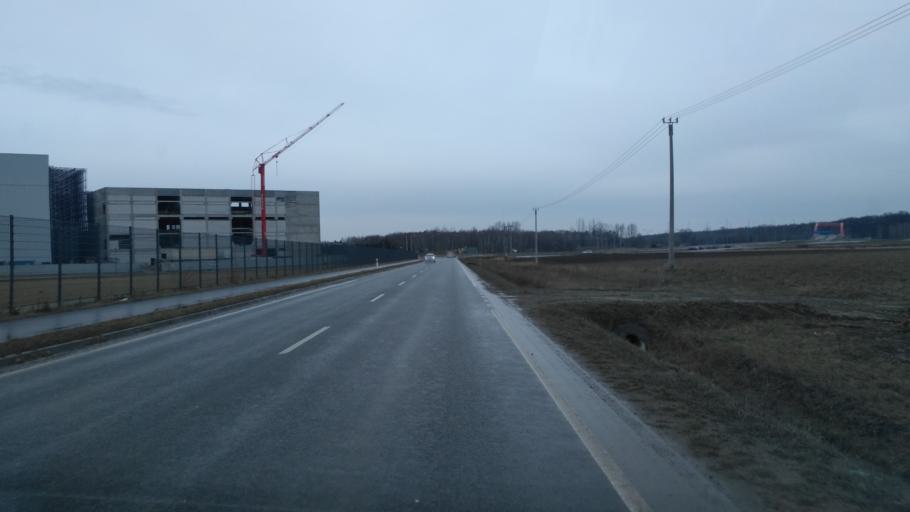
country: PL
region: Subcarpathian Voivodeship
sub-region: Powiat debicki
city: Brzeznica
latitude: 50.0721
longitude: 21.4703
